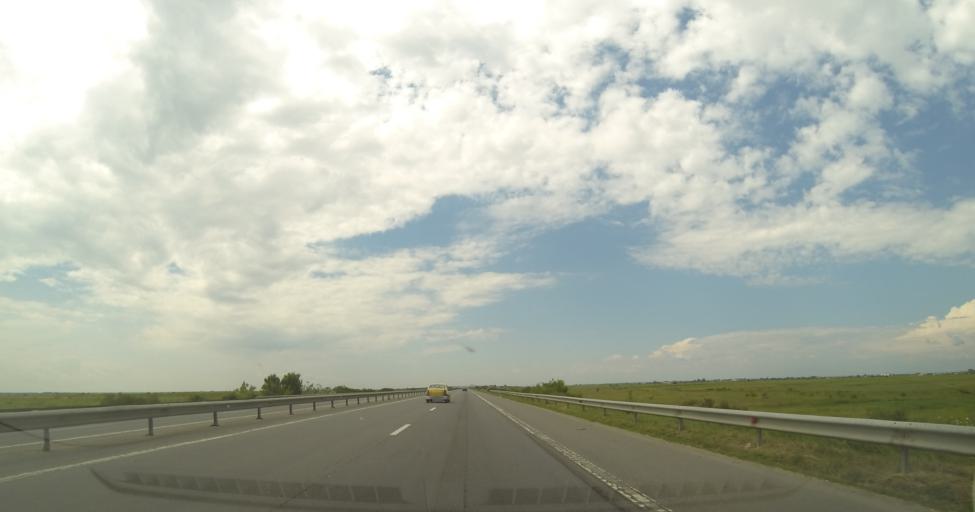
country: RO
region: Dambovita
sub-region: Comuna Petresti
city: Petresti
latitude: 44.6618
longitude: 25.3246
